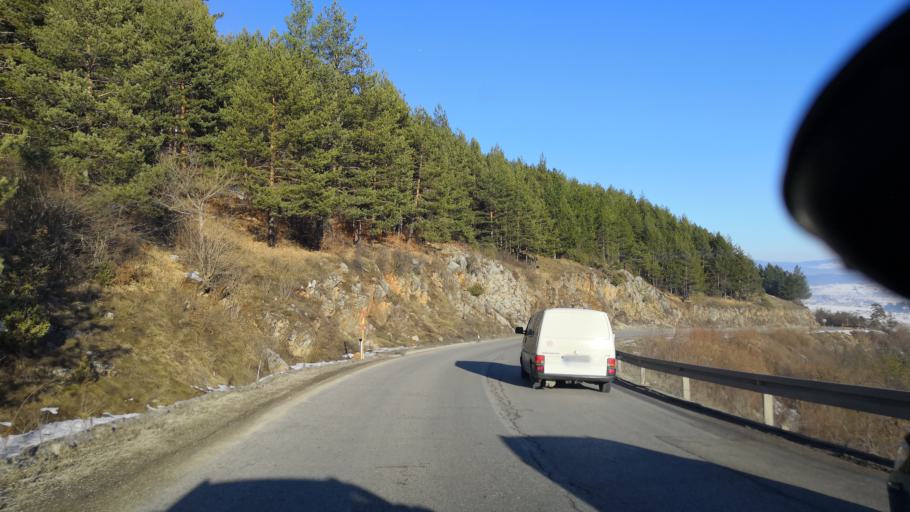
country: BA
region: Republika Srpska
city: Sokolac
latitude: 43.9179
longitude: 18.7348
